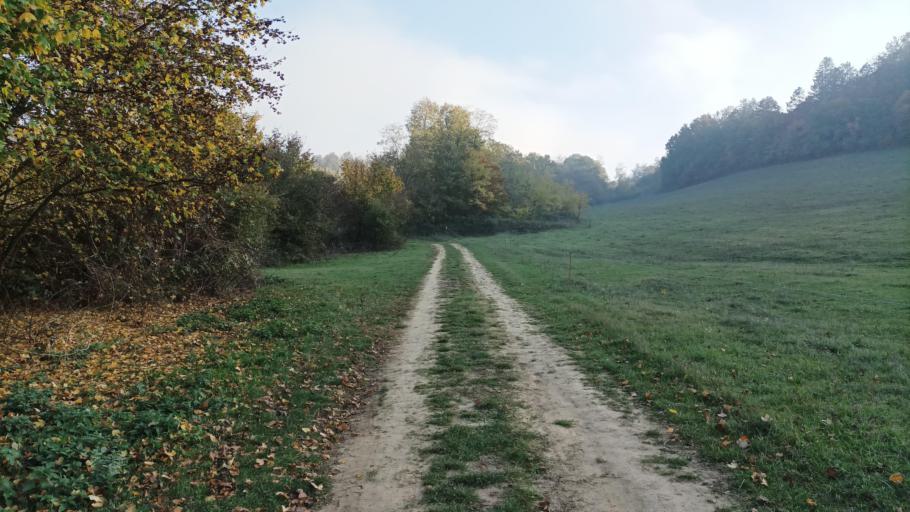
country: HU
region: Tolna
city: Szentgalpuszta
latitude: 46.3240
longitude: 18.6099
